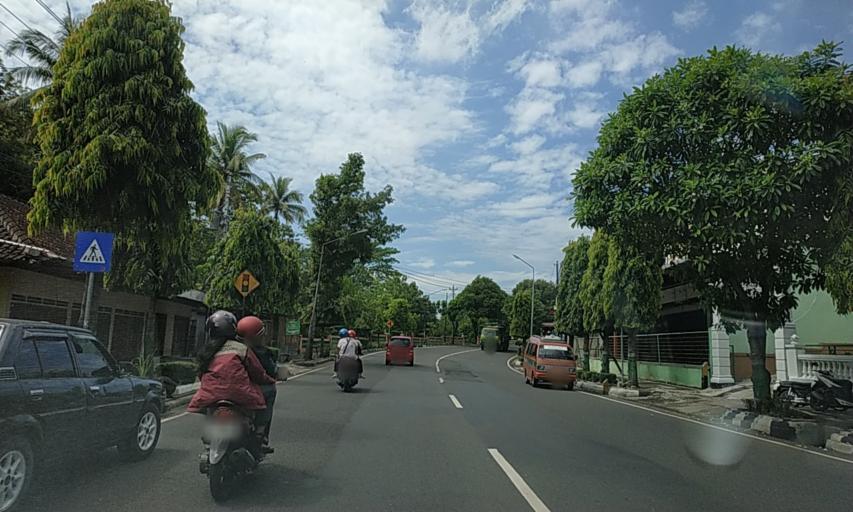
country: ID
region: Central Java
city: Selogiri
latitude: -7.8060
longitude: 110.9221
